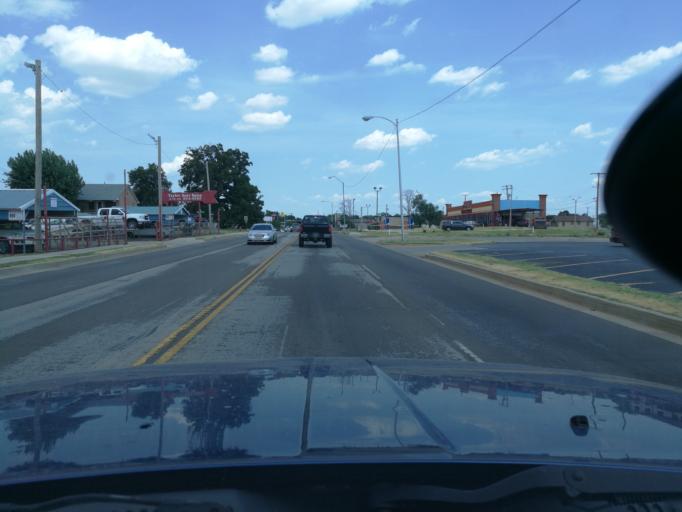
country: US
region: Oklahoma
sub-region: Oklahoma County
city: Oklahoma City
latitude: 35.4207
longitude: -97.5112
